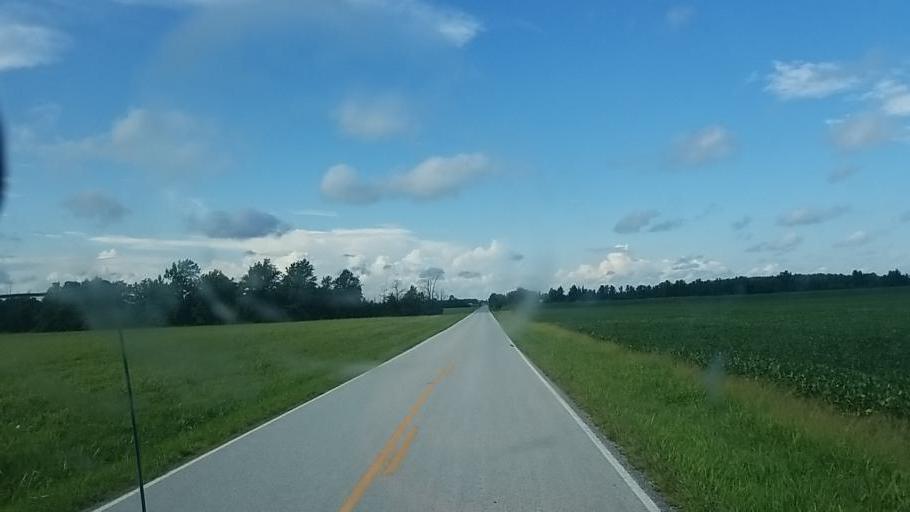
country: US
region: Ohio
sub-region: Hardin County
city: Forest
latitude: 40.7467
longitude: -83.4966
